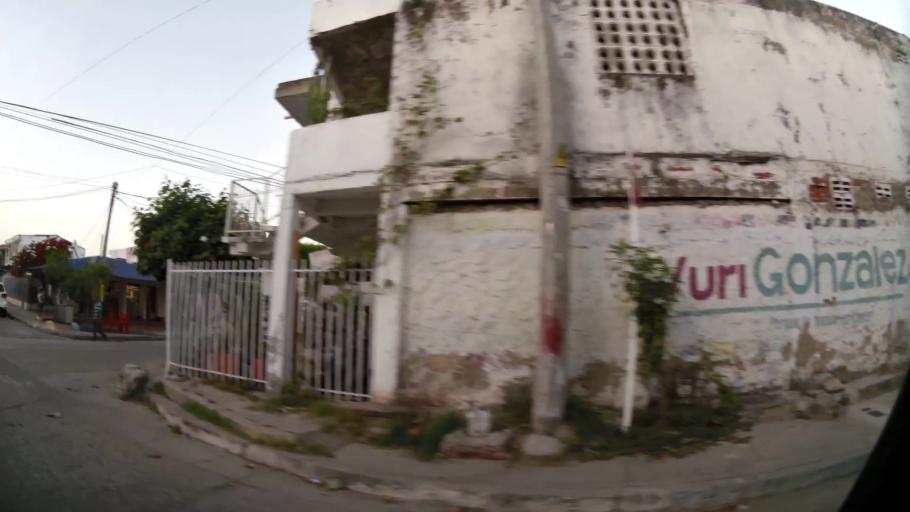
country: CO
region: Bolivar
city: Cartagena
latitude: 10.4050
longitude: -75.5164
